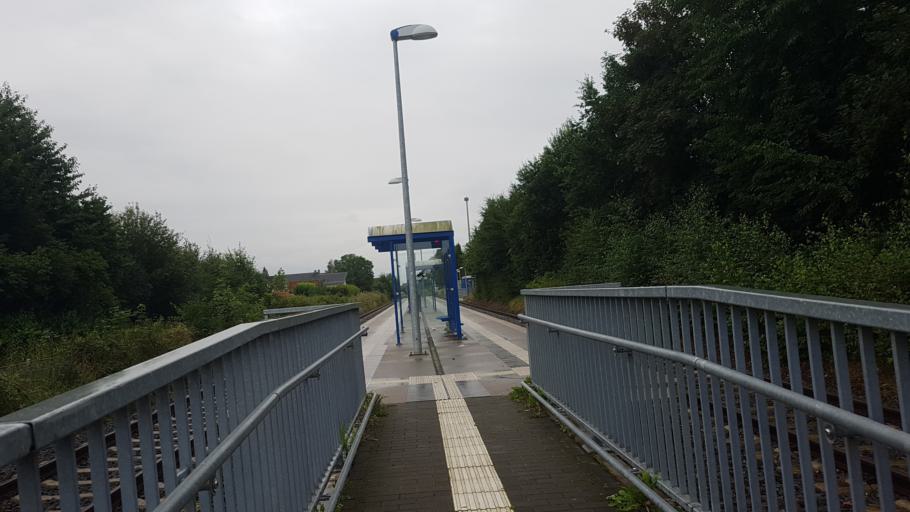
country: DE
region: North Rhine-Westphalia
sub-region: Regierungsbezirk Koln
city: Niederzier
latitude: 50.8536
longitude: 6.4523
